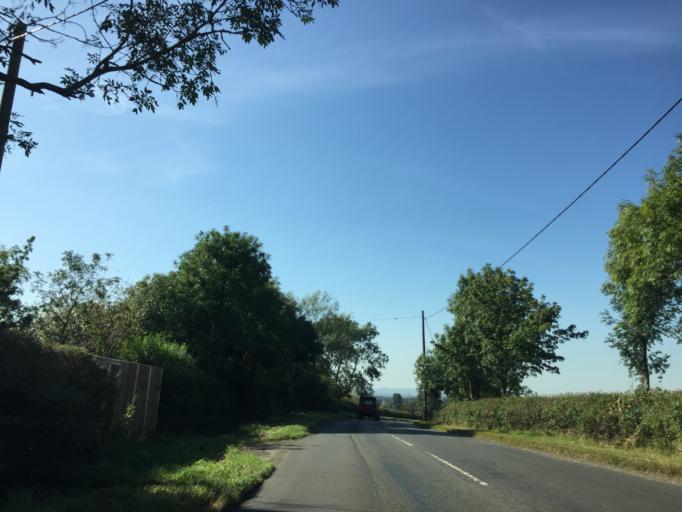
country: GB
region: England
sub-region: Leicestershire
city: Queniborough
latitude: 52.6985
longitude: -1.0064
